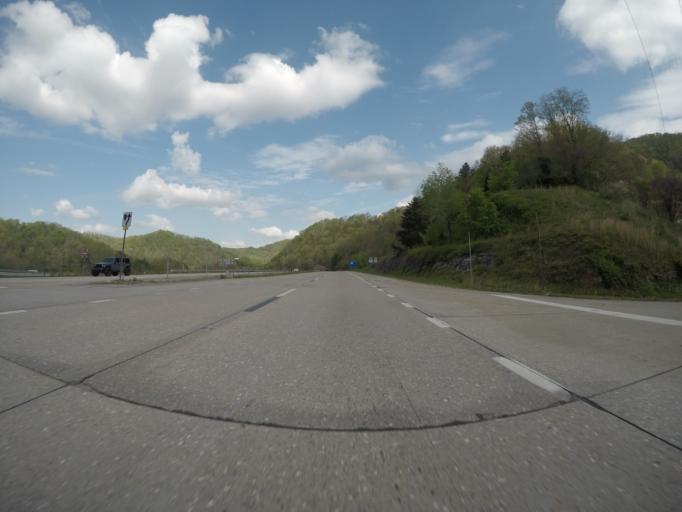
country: US
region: West Virginia
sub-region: Boone County
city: Madison
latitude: 38.1024
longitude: -81.8412
